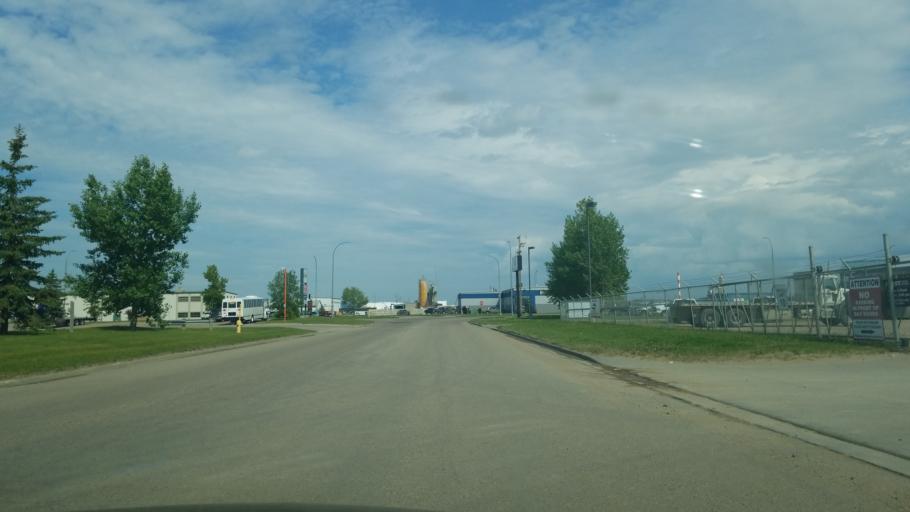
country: CA
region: Saskatchewan
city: Lloydminster
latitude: 53.2914
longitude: -110.0359
